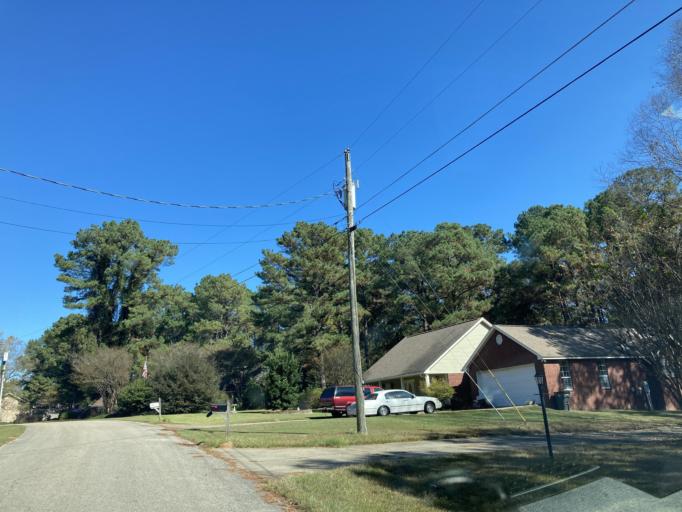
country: US
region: Mississippi
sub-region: Lamar County
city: West Hattiesburg
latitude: 31.2690
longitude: -89.4142
